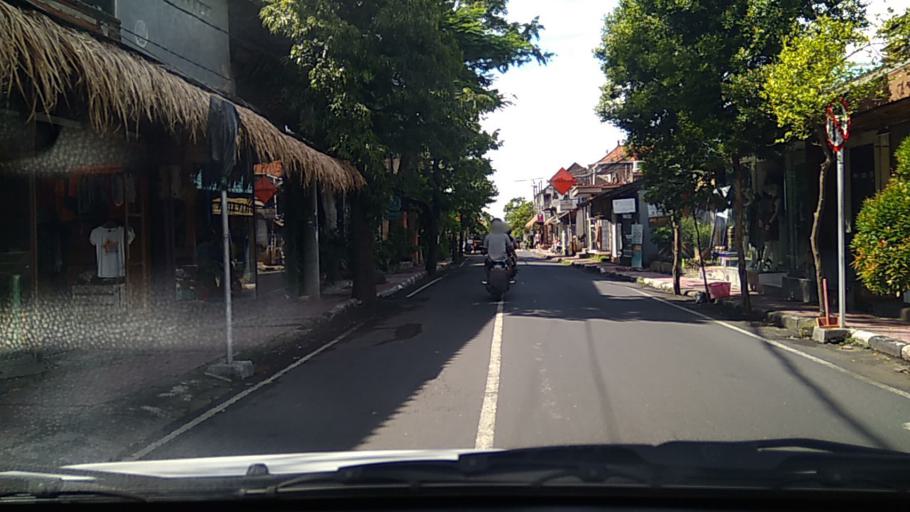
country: ID
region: Bali
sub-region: Kabupaten Gianyar
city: Ubud
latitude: -8.5135
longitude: 115.2641
